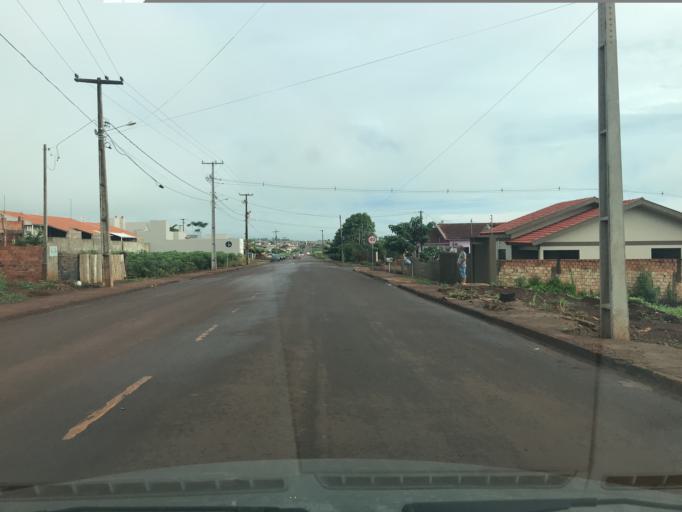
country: BR
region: Parana
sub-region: Palotina
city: Palotina
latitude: -24.2991
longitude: -53.8423
